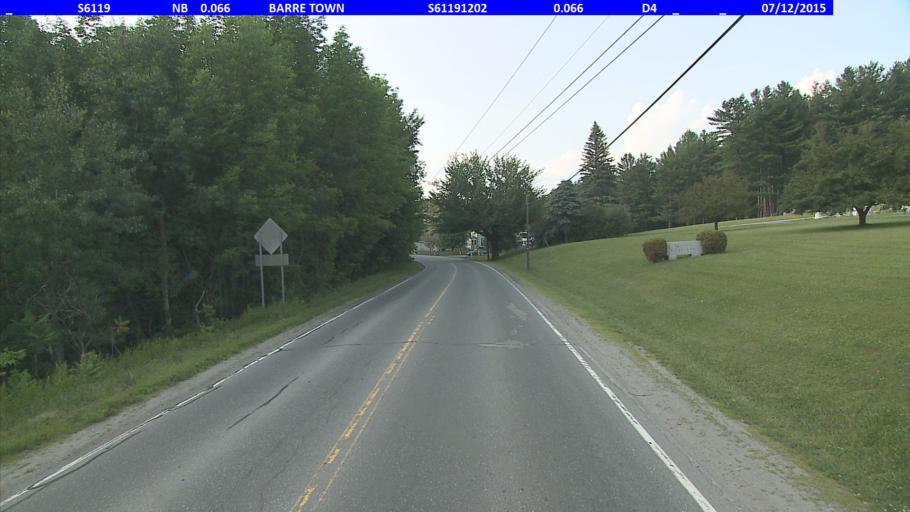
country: US
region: Vermont
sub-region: Washington County
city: South Barre
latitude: 44.1711
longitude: -72.4914
